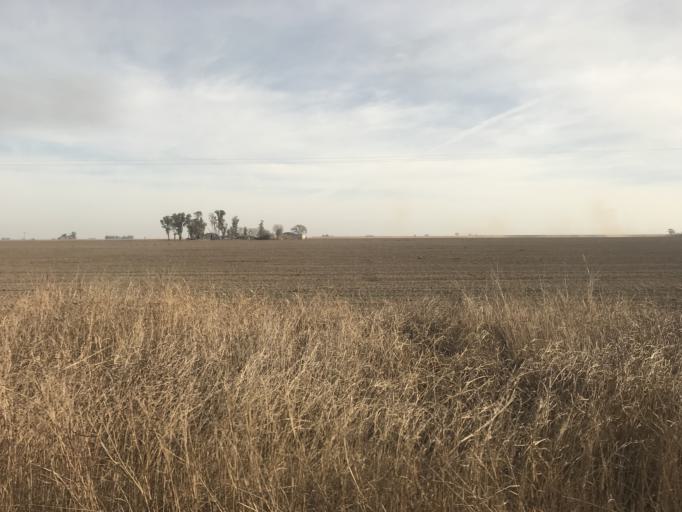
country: AR
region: Cordoba
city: Laguna Larga
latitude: -31.7498
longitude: -63.8268
